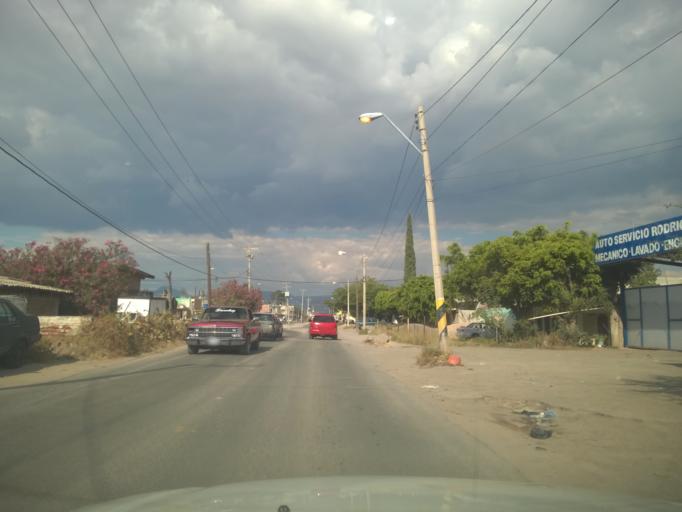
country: MX
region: Guanajuato
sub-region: Leon
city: San Jose de Duran (Los Troncoso)
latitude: 21.0718
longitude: -101.6212
